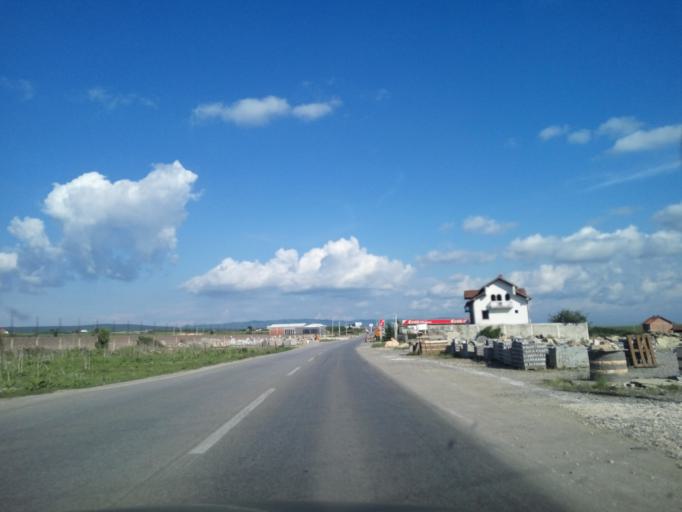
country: XK
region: Prizren
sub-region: Komuna e Malisheves
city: Llazice
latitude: 42.5767
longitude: 20.7055
